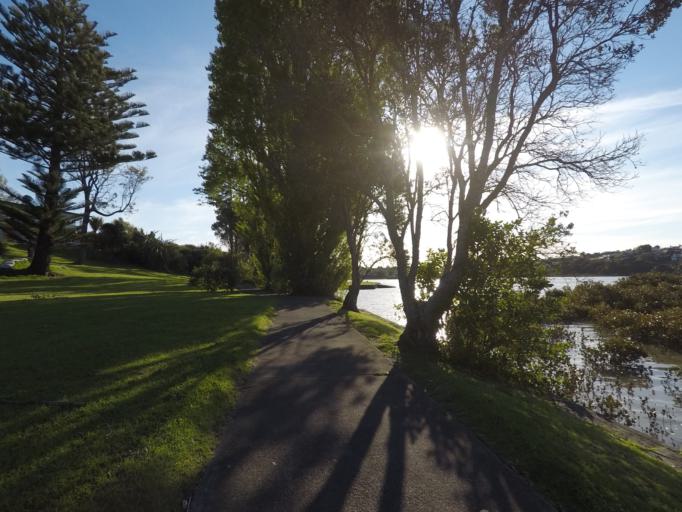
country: NZ
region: Auckland
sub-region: Auckland
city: Rosebank
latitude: -36.8252
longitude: 174.6457
